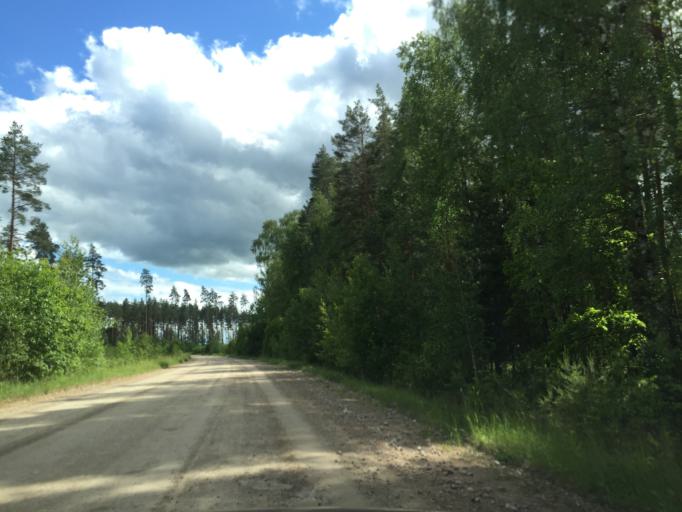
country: LV
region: Vecumnieki
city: Vecumnieki
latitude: 56.4884
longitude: 24.4081
